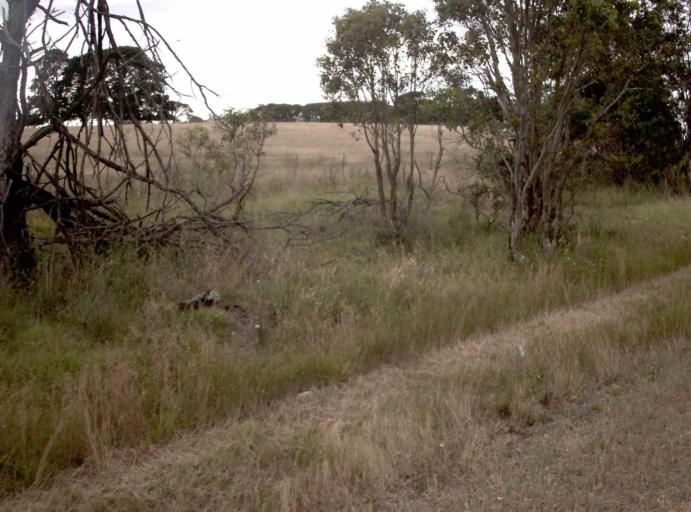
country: AU
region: Victoria
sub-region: Wellington
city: Sale
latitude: -37.9949
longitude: 147.2054
